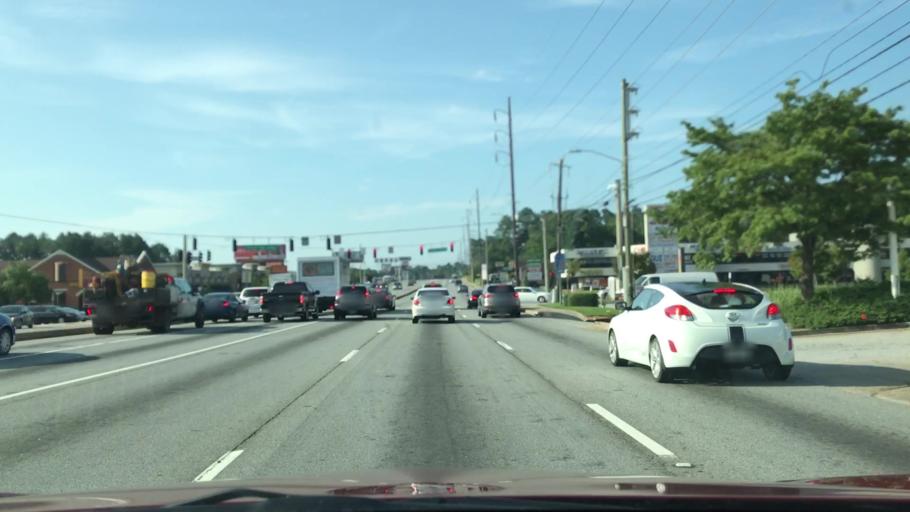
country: US
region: Georgia
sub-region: Gwinnett County
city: Norcross
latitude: 33.9081
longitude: -84.2063
